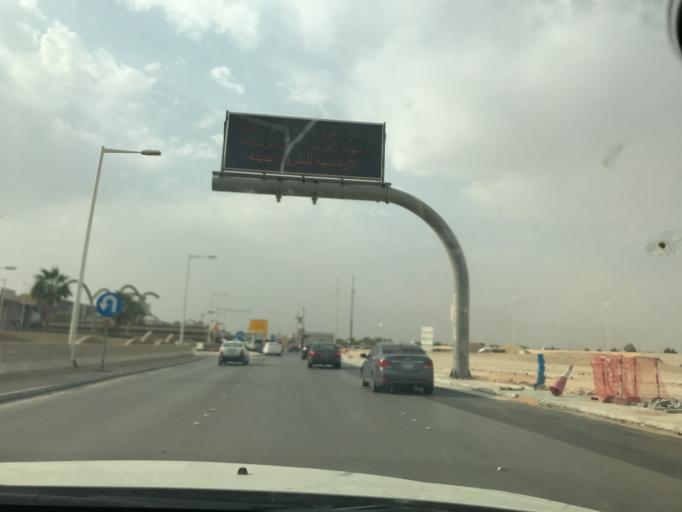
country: SA
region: Ar Riyad
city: Riyadh
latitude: 24.7201
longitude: 46.6938
